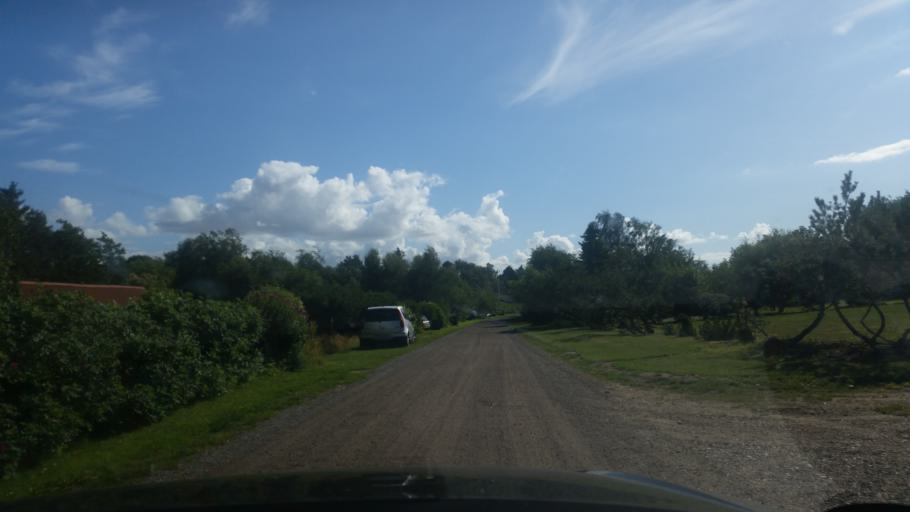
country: DK
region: Zealand
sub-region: Odsherred Kommune
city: Horve
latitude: 55.8115
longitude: 11.4110
